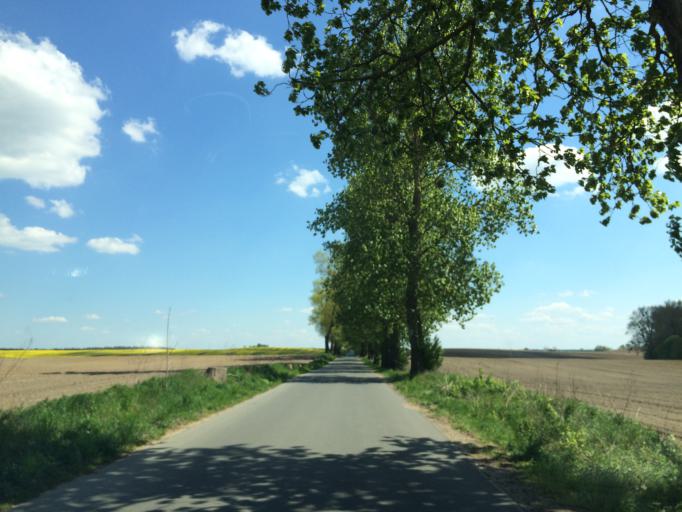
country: PL
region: Warmian-Masurian Voivodeship
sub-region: Powiat nowomiejski
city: Biskupiec
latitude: 53.4329
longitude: 19.2773
